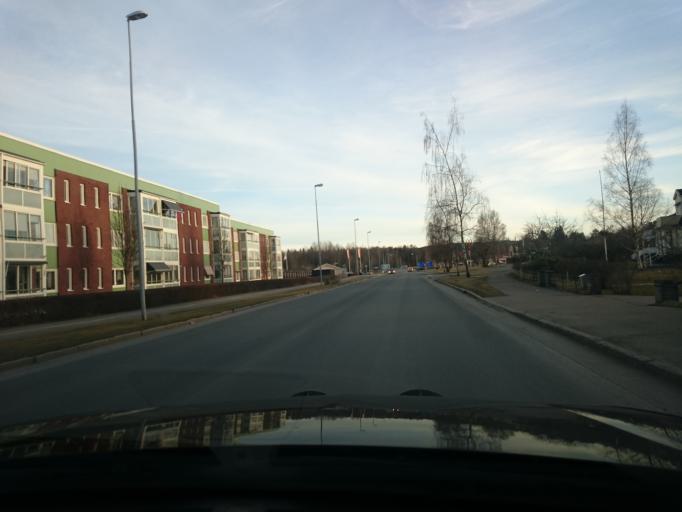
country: SE
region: Joenkoeping
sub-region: Vetlanda Kommun
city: Vetlanda
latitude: 57.4176
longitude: 15.0912
